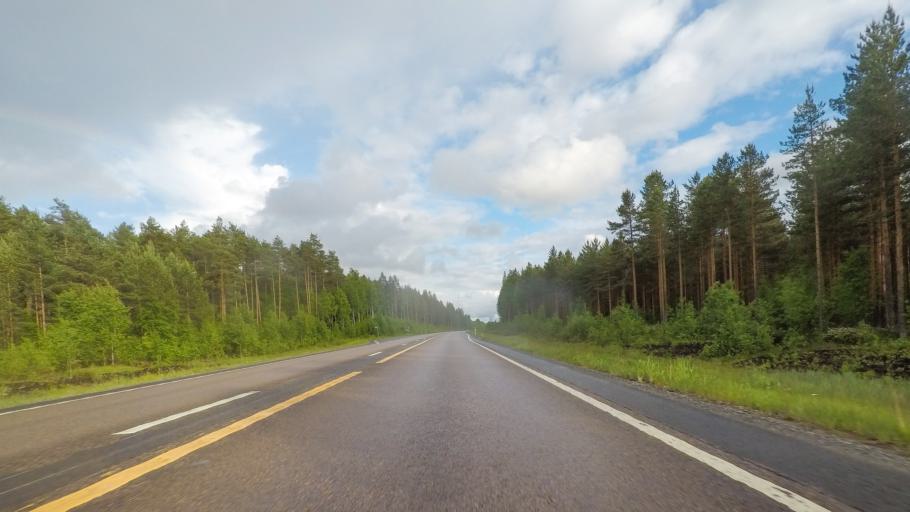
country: FI
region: Paijanne Tavastia
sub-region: Lahti
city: Hartola
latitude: 61.4367
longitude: 26.0014
